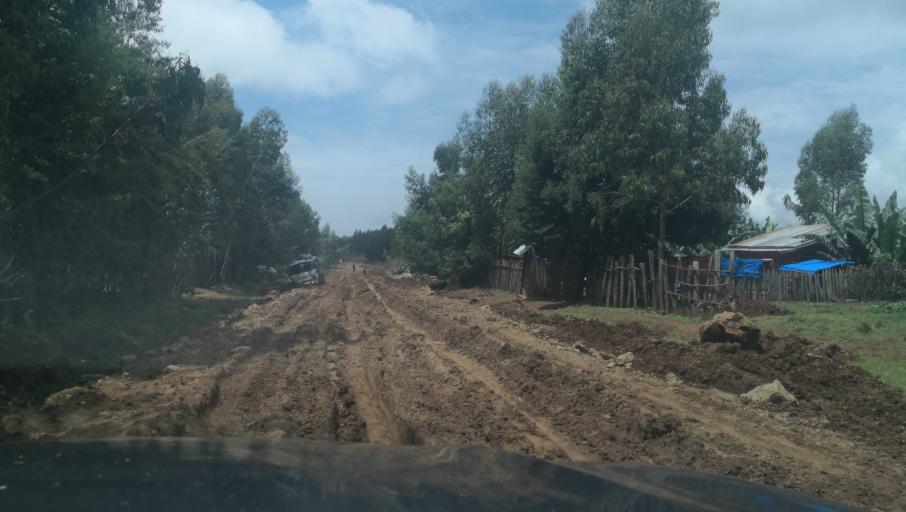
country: ET
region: Southern Nations, Nationalities, and People's Region
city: Butajira
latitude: 8.2897
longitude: 38.4727
